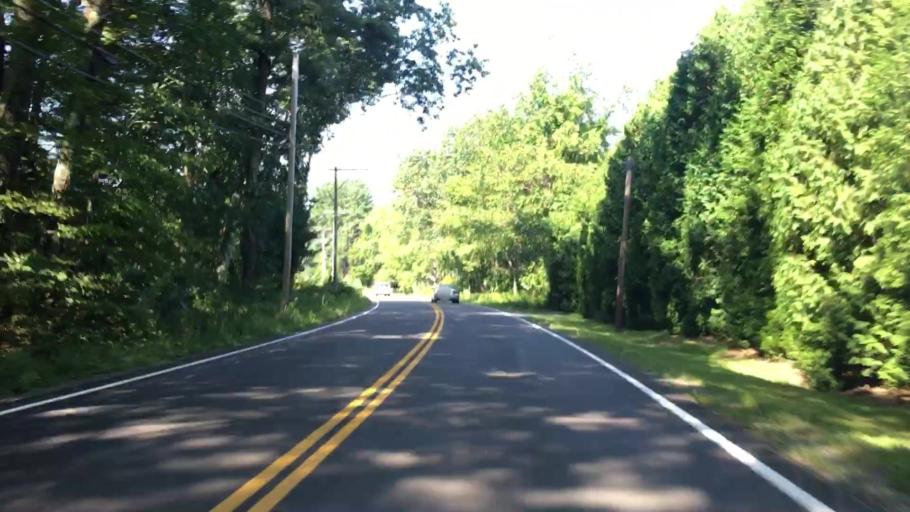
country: US
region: New Hampshire
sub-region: Rockingham County
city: Kingston
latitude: 42.9308
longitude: -71.0387
